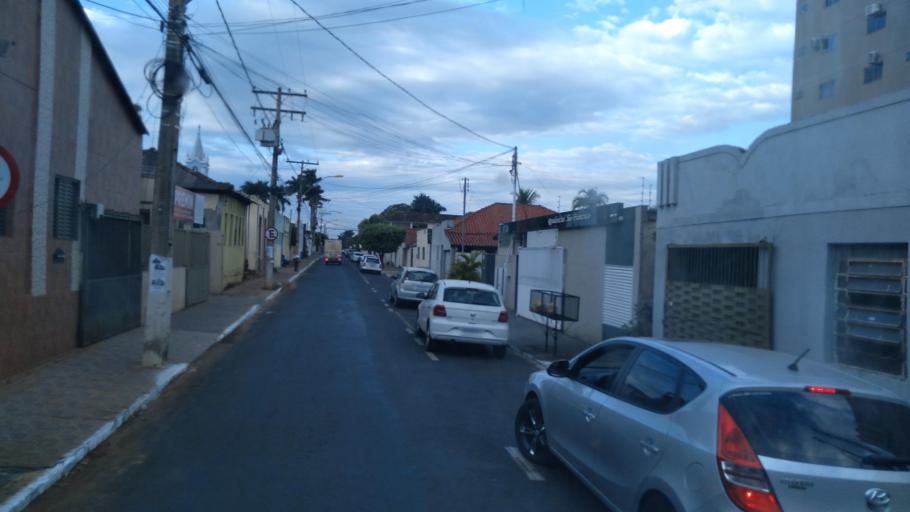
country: BR
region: Goias
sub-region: Mineiros
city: Mineiros
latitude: -17.5711
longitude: -52.5537
